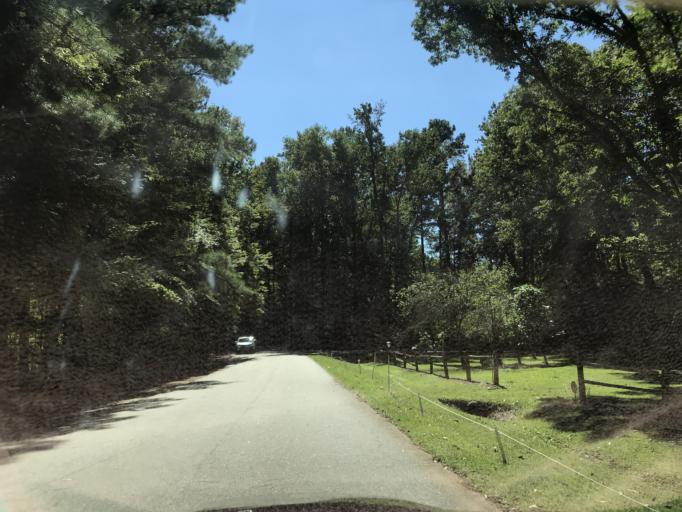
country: US
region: North Carolina
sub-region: Wake County
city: Wake Forest
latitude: 35.9456
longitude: -78.5903
